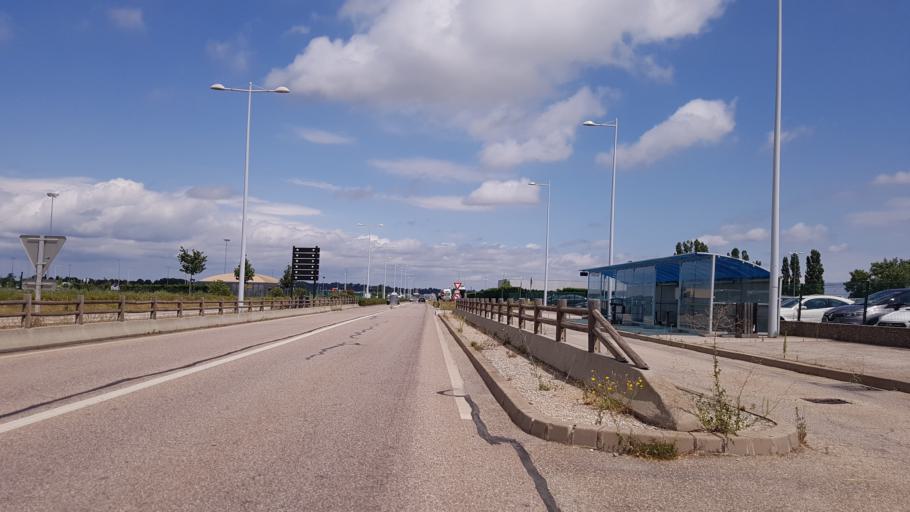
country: FR
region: Rhone-Alpes
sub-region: Departement du Rhone
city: Pusignan
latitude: 45.7243
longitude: 5.0723
